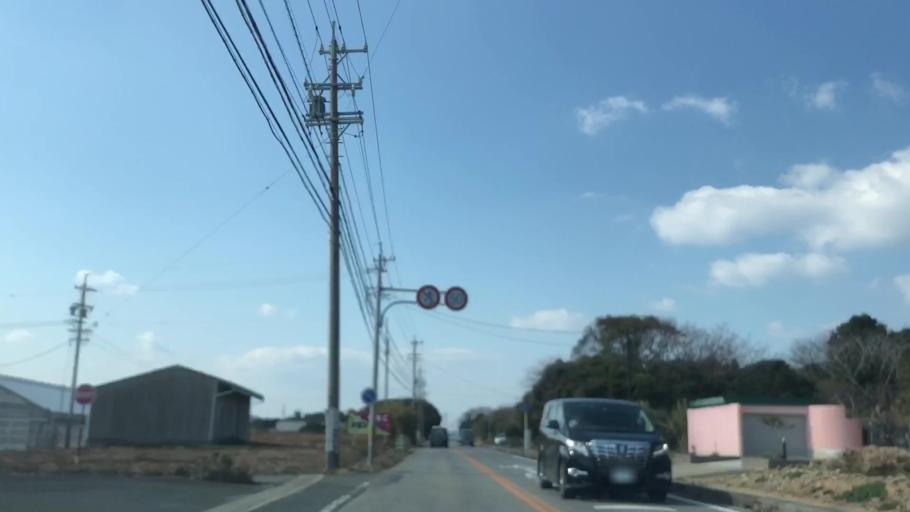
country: JP
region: Aichi
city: Tahara
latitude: 34.5907
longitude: 137.1052
